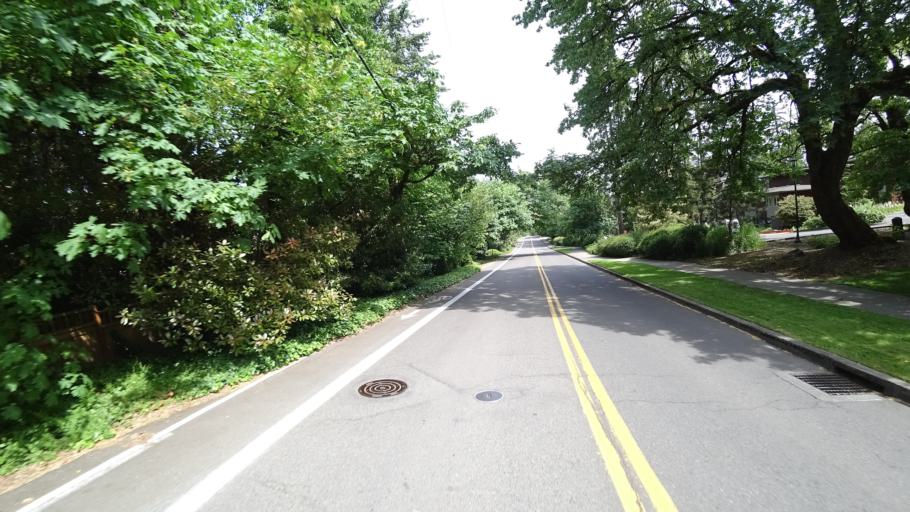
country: US
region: Oregon
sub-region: Clackamas County
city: Lake Oswego
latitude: 45.4470
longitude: -122.6728
